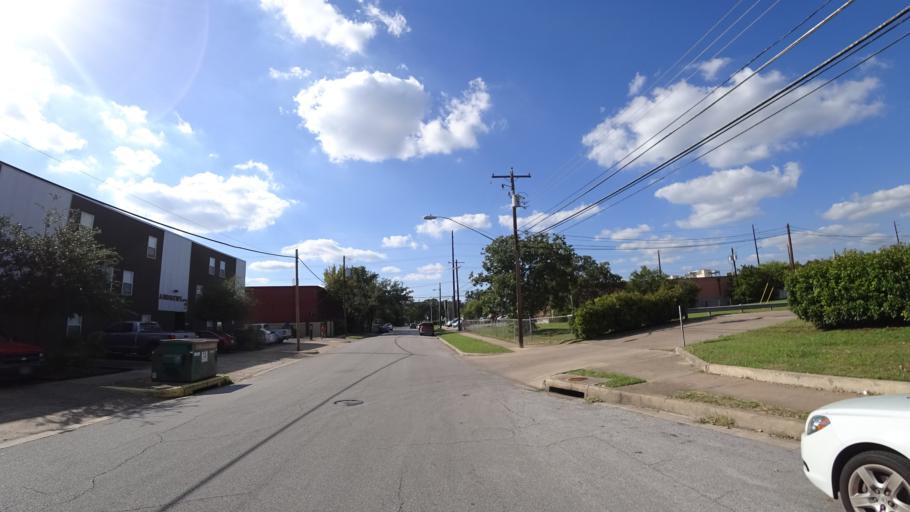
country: US
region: Texas
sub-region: Travis County
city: Austin
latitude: 30.3036
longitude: -97.7363
